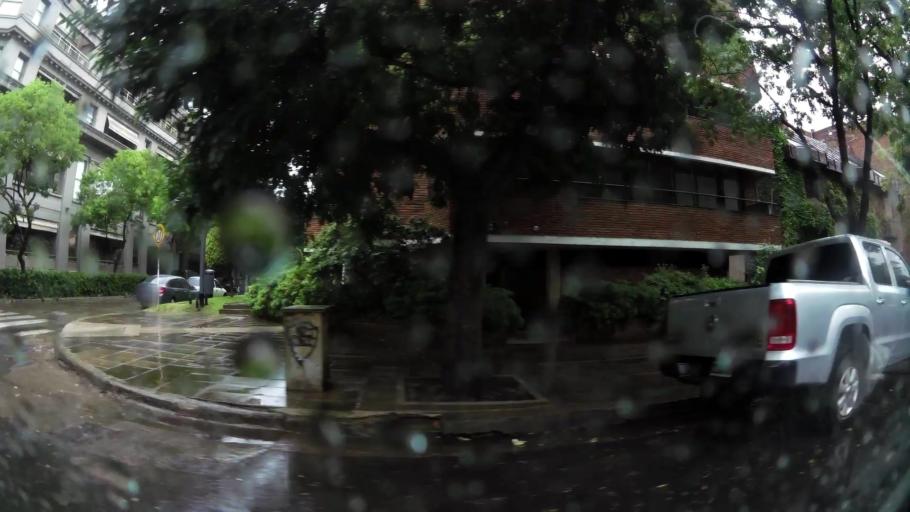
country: AR
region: Buenos Aires F.D.
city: Retiro
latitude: -34.5768
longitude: -58.4019
